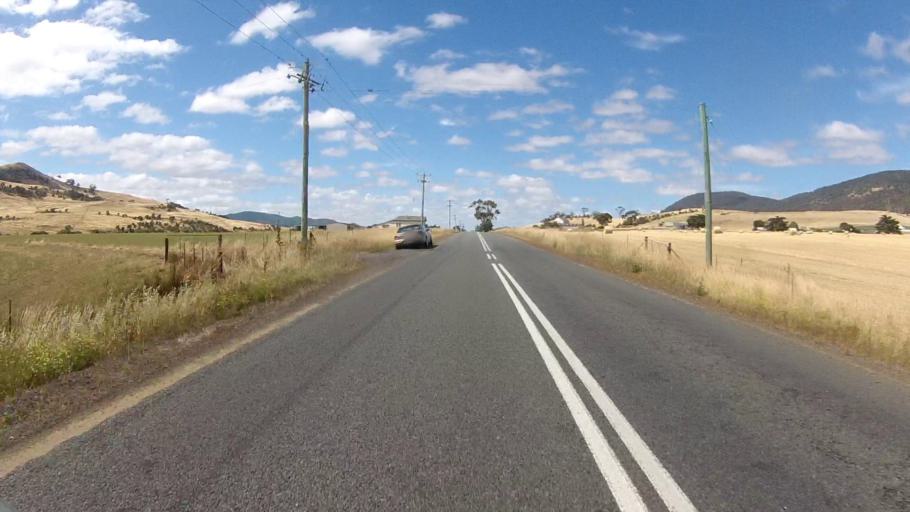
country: AU
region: Tasmania
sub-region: Brighton
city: Bridgewater
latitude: -42.5892
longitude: 147.4093
